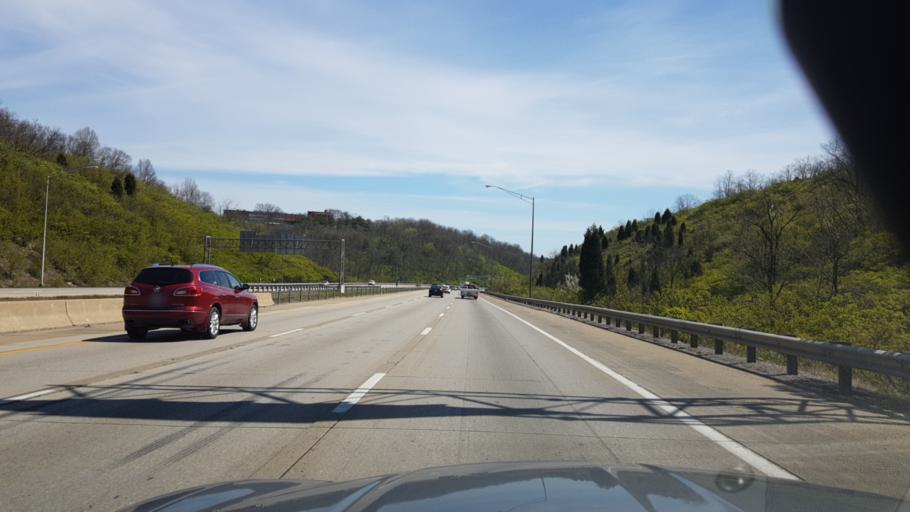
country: US
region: Kentucky
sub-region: Kenton County
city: Lakeside Park
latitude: 39.0256
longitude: -84.5585
